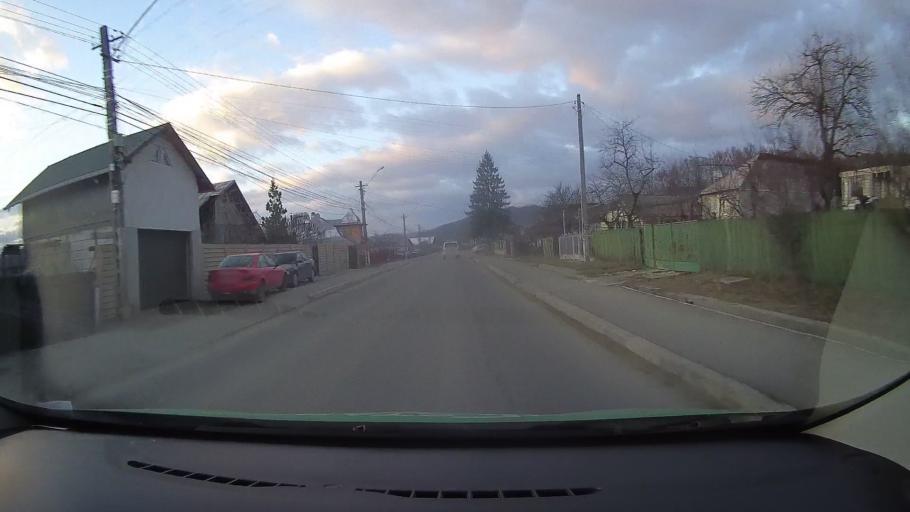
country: RO
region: Dambovita
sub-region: Municipiul Moreni
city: Moreni
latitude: 45.0001
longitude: 25.6473
